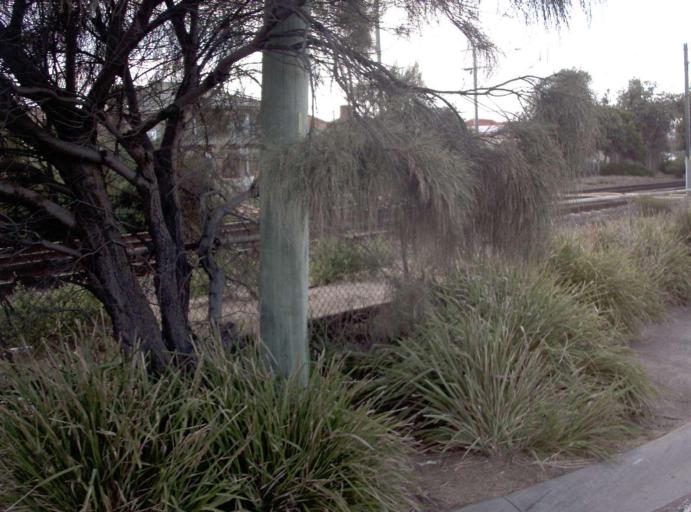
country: AU
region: Victoria
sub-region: Kingston
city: Edithvale
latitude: -38.0364
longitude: 145.1073
